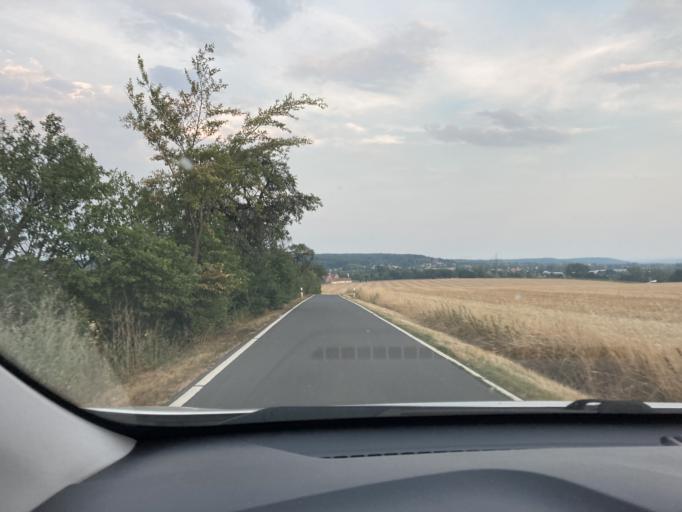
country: DE
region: Saxony
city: Niederau
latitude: 51.1887
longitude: 13.5436
